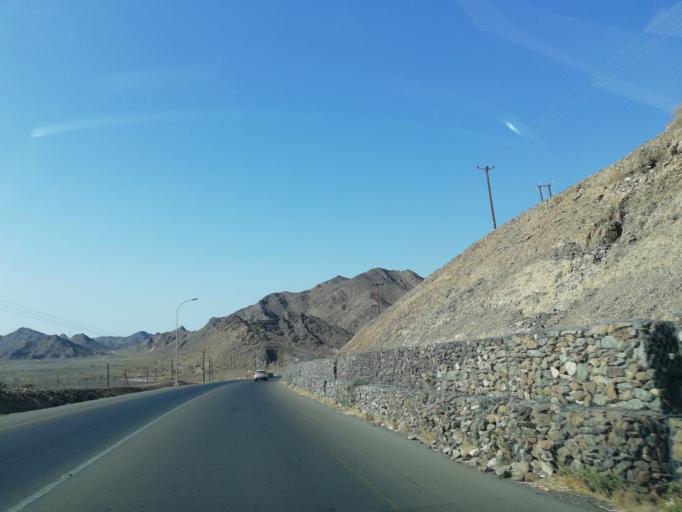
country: OM
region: Ash Sharqiyah
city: Ibra'
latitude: 22.8106
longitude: 58.1690
